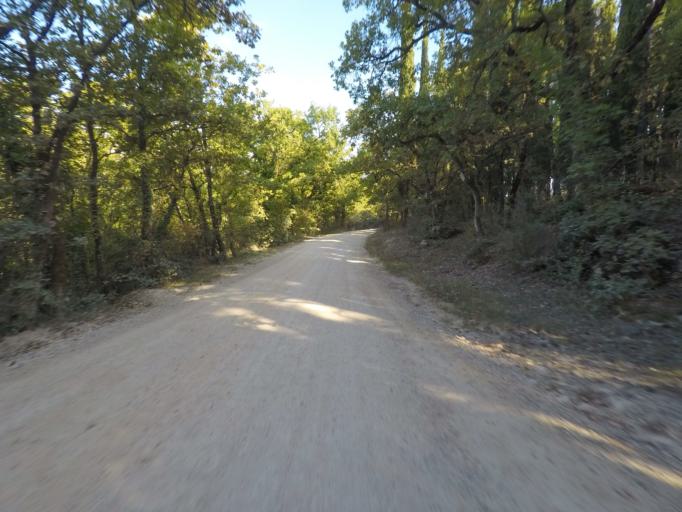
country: IT
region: Tuscany
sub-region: Provincia di Siena
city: Castellina in Chianti
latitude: 43.4371
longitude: 11.3114
